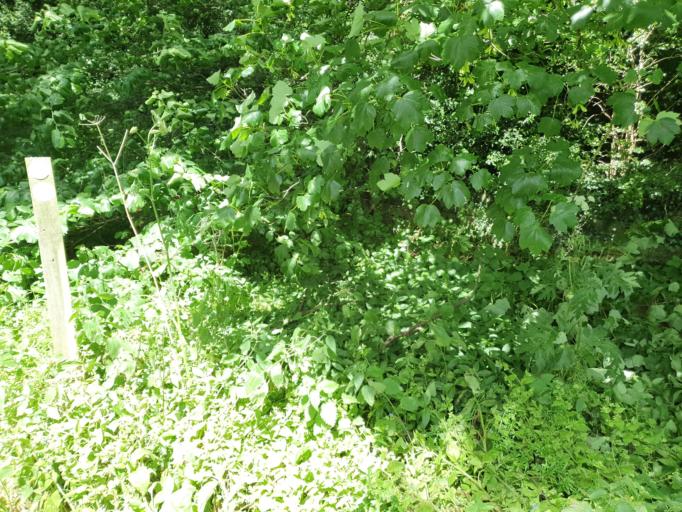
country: GB
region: England
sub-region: City and Borough of Leeds
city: Guiseley
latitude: 53.8621
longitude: -1.7378
